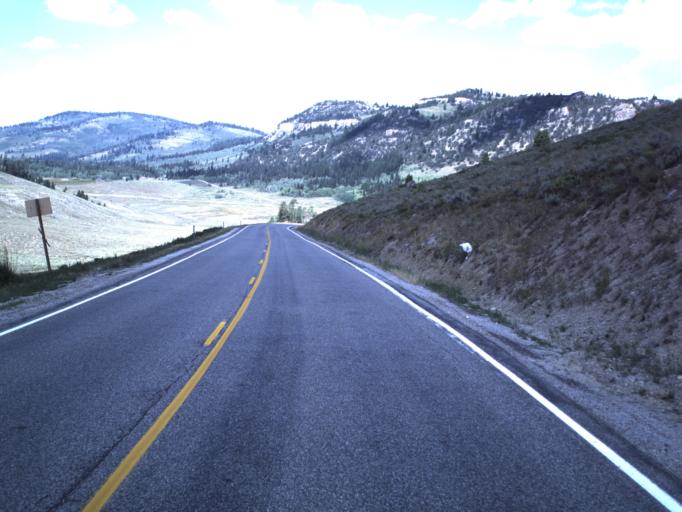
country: US
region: Idaho
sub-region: Bear Lake County
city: Paris
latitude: 41.9374
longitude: -111.4812
